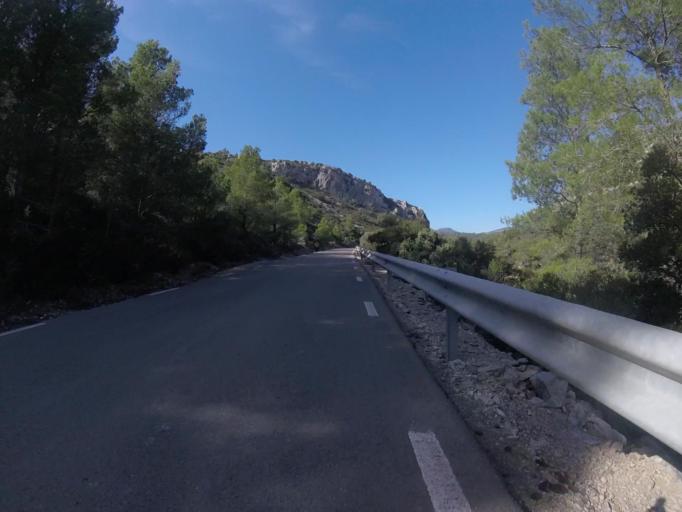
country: ES
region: Valencia
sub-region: Provincia de Castello
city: Sarratella
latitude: 40.2723
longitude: 0.0469
